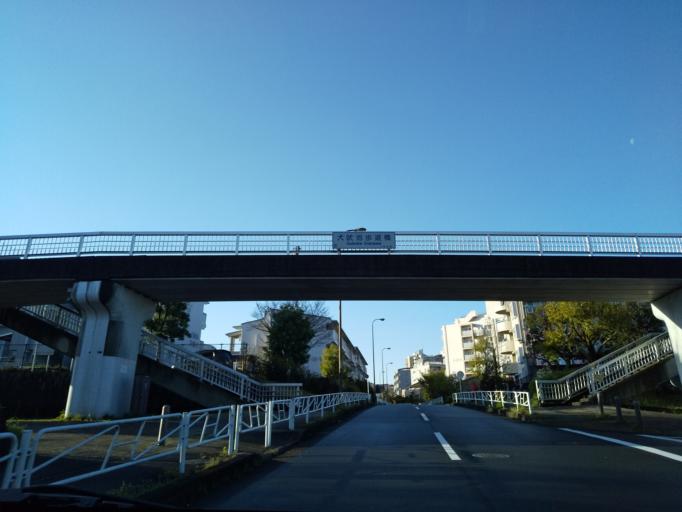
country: JP
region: Tokyo
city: Hachioji
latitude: 35.6154
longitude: 139.3679
